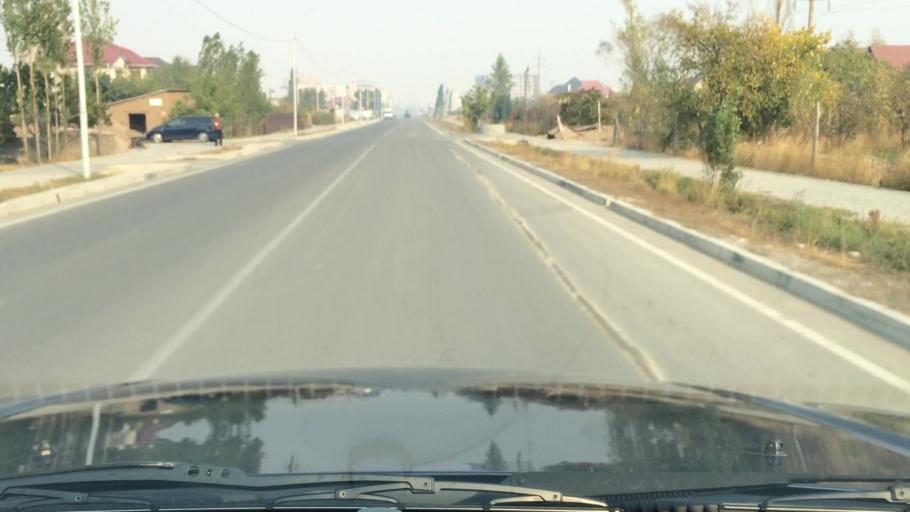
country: KG
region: Chuy
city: Bishkek
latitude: 42.8229
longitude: 74.5699
